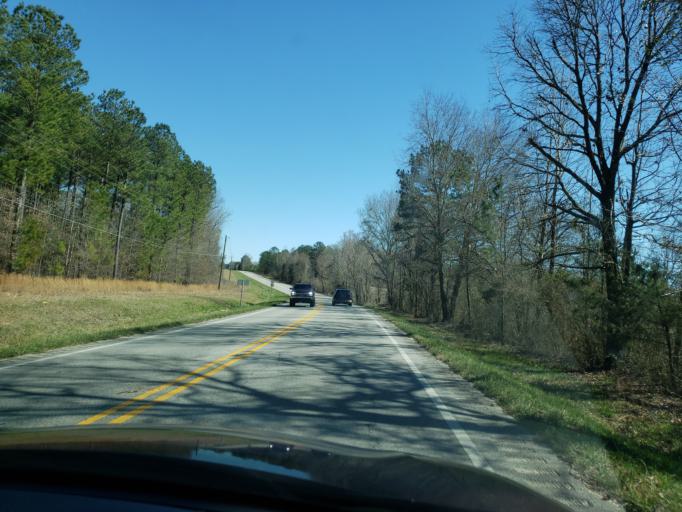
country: US
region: Alabama
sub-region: Lee County
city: Auburn
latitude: 32.5992
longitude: -85.5781
